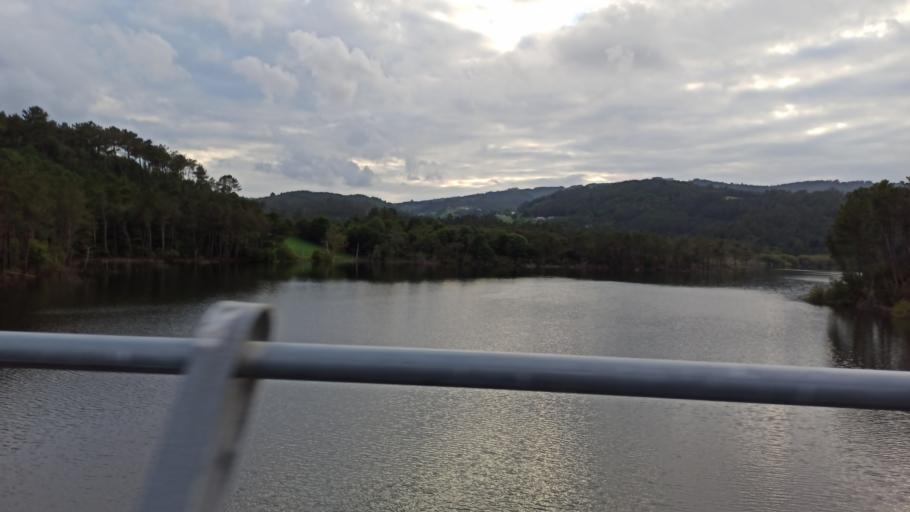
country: ES
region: Galicia
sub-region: Provincia da Coruna
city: Santiso
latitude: 42.8200
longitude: -8.1263
